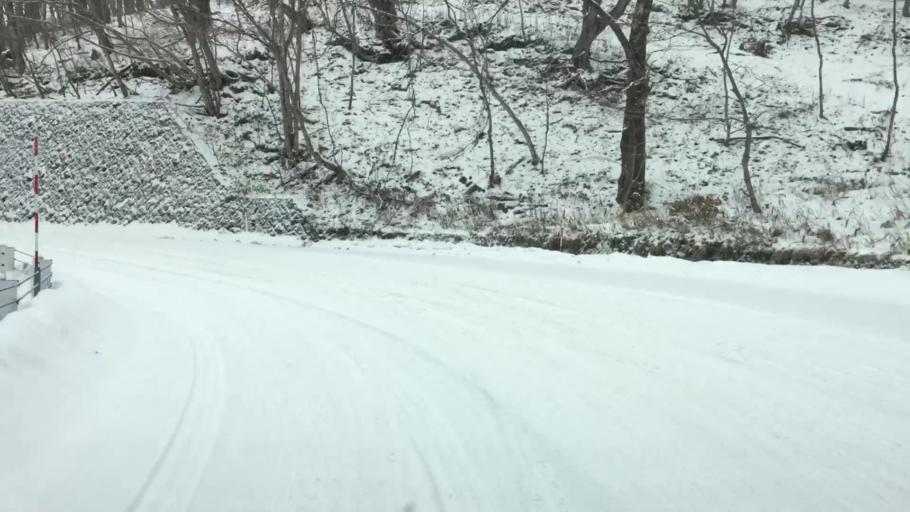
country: JP
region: Tochigi
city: Imaichi
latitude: 36.9063
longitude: 139.7421
